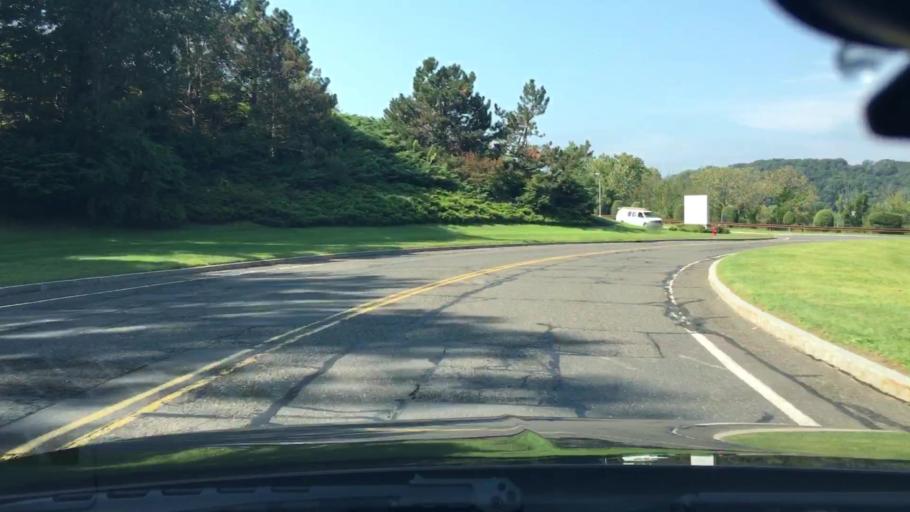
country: US
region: Connecticut
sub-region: Fairfield County
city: Danbury
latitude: 41.4263
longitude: -73.4101
